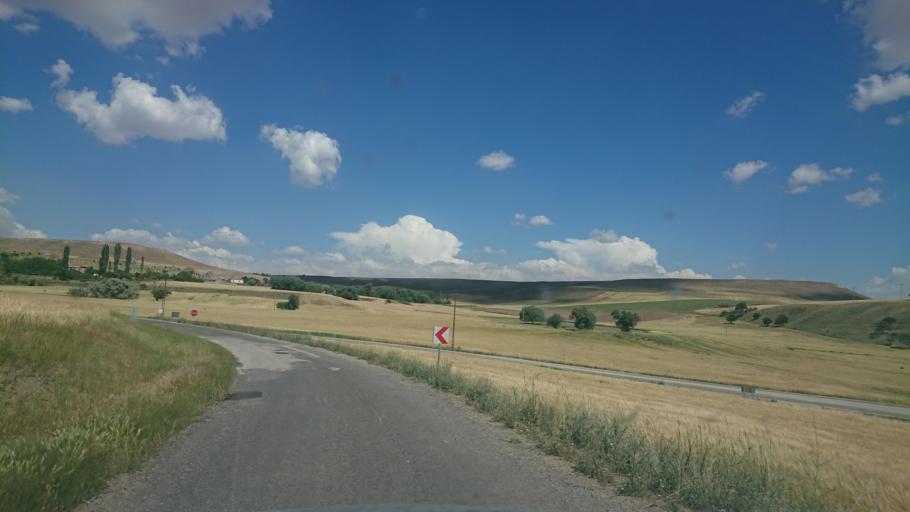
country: TR
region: Aksaray
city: Agacoren
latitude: 38.7997
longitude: 33.8237
